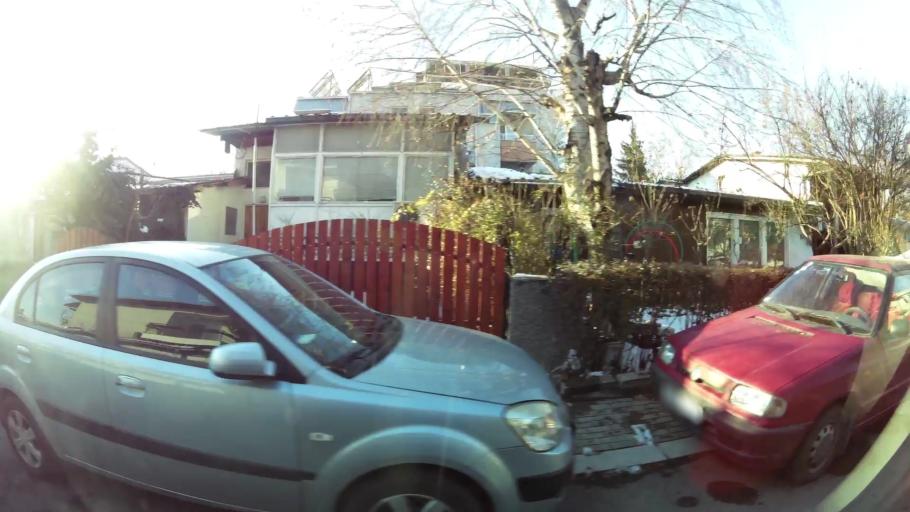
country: MK
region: Karpos
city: Skopje
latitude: 42.0024
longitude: 21.3929
